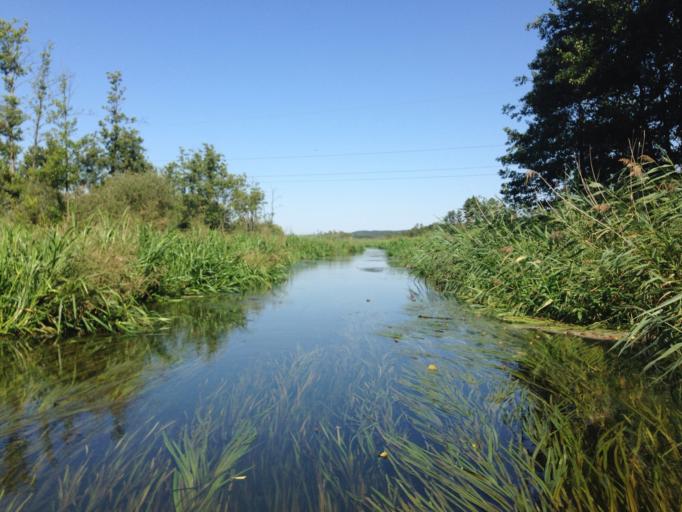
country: PL
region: Kujawsko-Pomorskie
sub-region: Powiat brodnicki
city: Bartniczka
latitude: 53.2616
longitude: 19.5994
